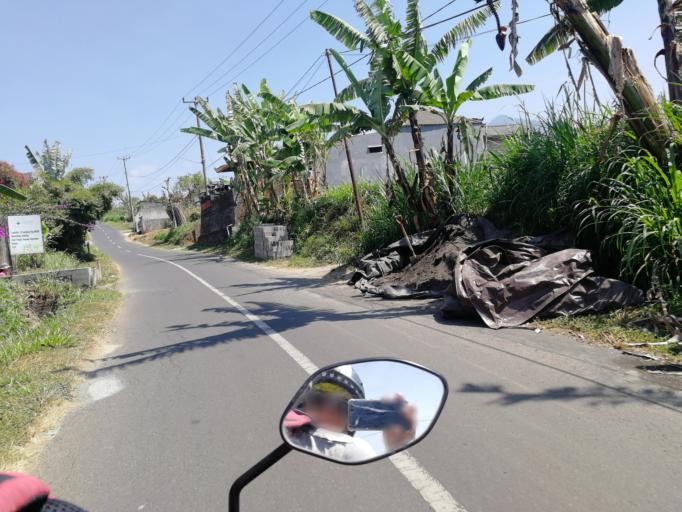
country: ID
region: Bali
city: Peneng
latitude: -8.3027
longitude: 115.1824
